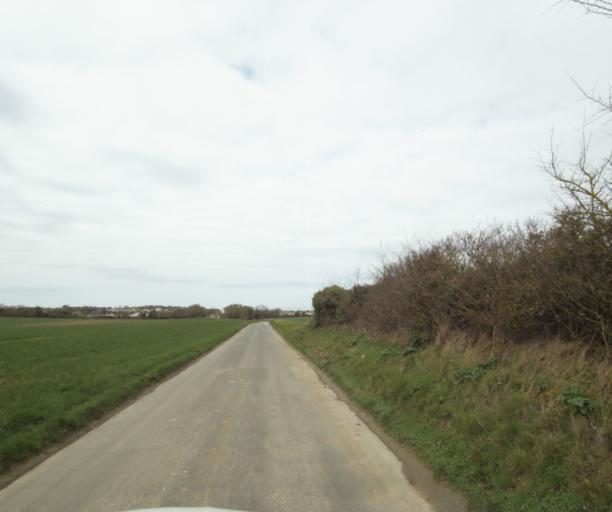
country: FR
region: Poitou-Charentes
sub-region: Departement de la Charente-Maritime
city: Nieul-sur-Mer
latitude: 46.1899
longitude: -1.1709
